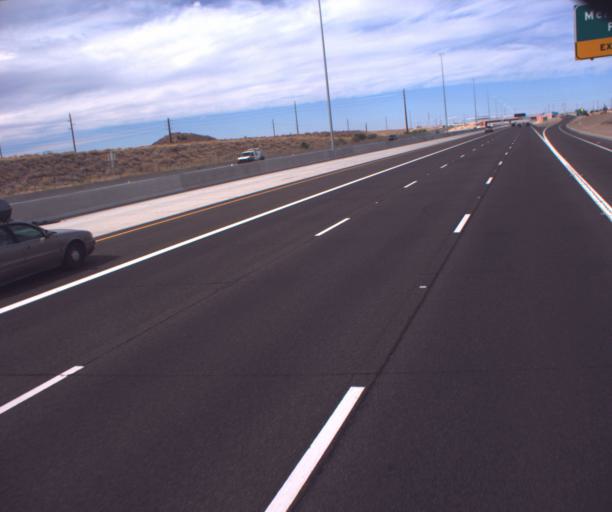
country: US
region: Arizona
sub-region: Pinal County
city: Apache Junction
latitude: 33.4463
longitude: -111.6636
